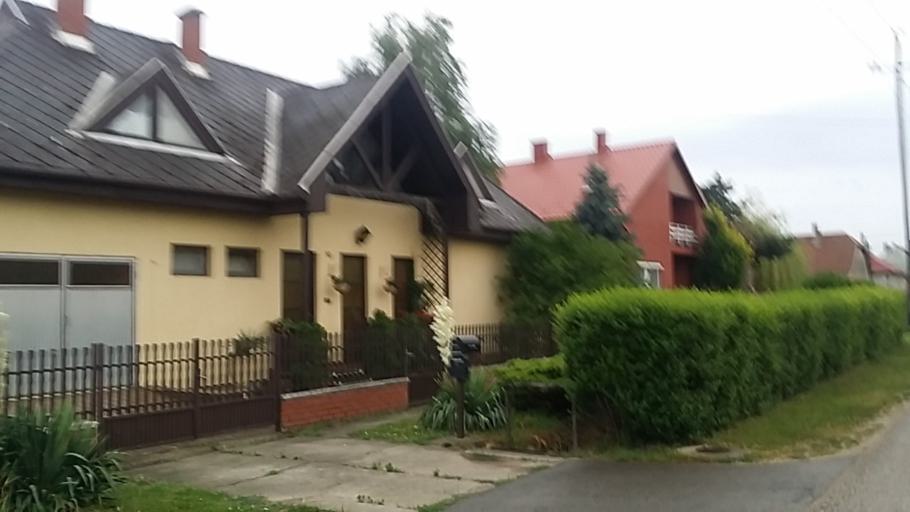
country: HU
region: Tolna
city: Tolna
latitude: 46.4150
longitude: 18.7587
